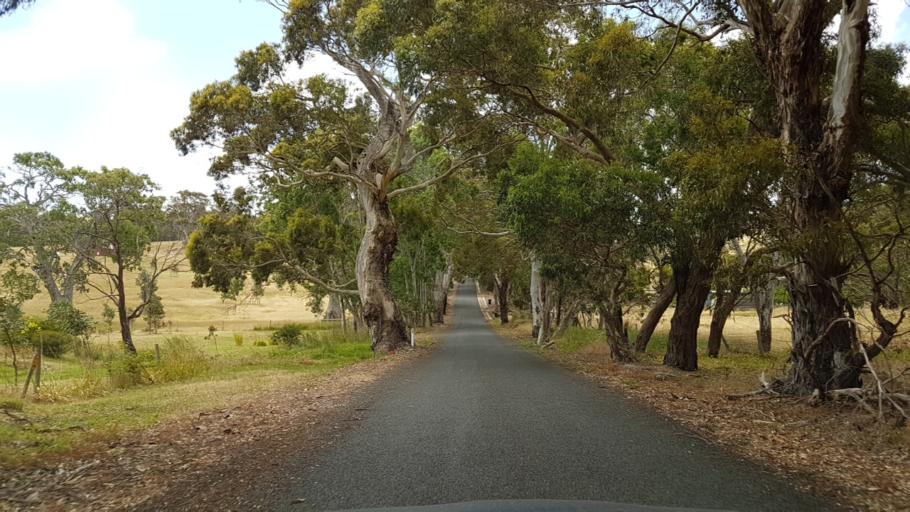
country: AU
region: South Australia
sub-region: Victor Harbor
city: Victor Harbor
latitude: -35.4660
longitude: 138.5946
